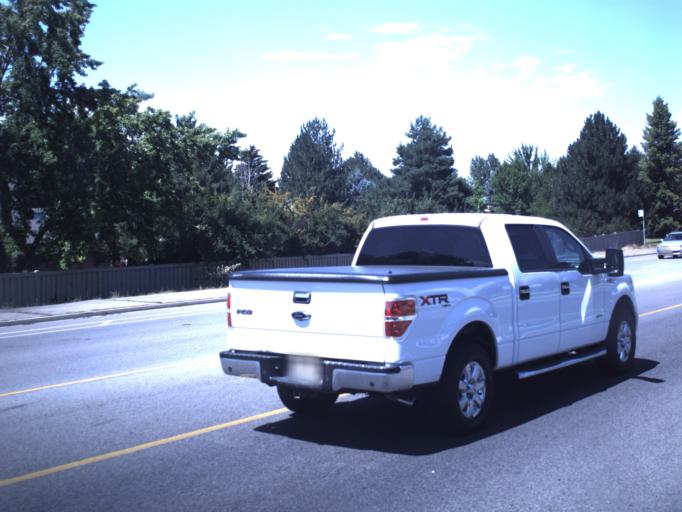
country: US
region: Utah
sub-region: Utah County
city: Provo
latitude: 40.2759
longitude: -111.6574
